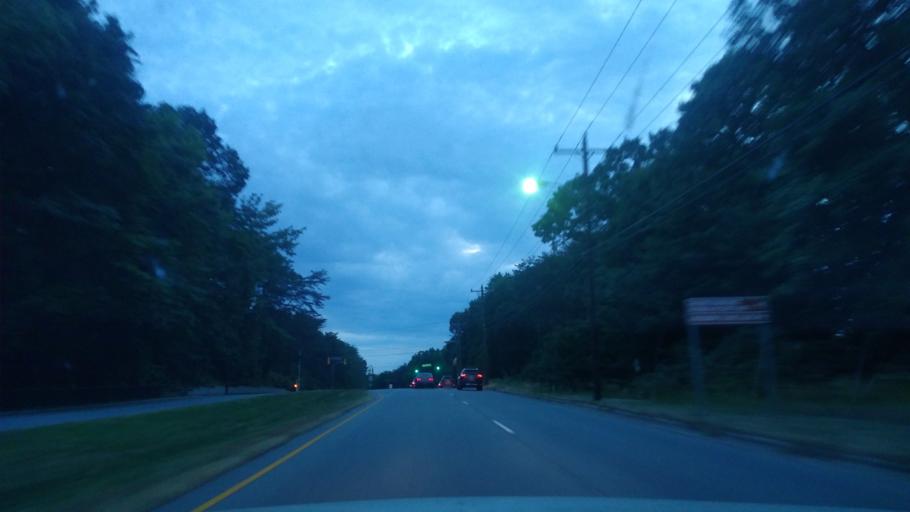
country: US
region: North Carolina
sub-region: Guilford County
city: Greensboro
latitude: 36.1108
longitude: -79.7870
